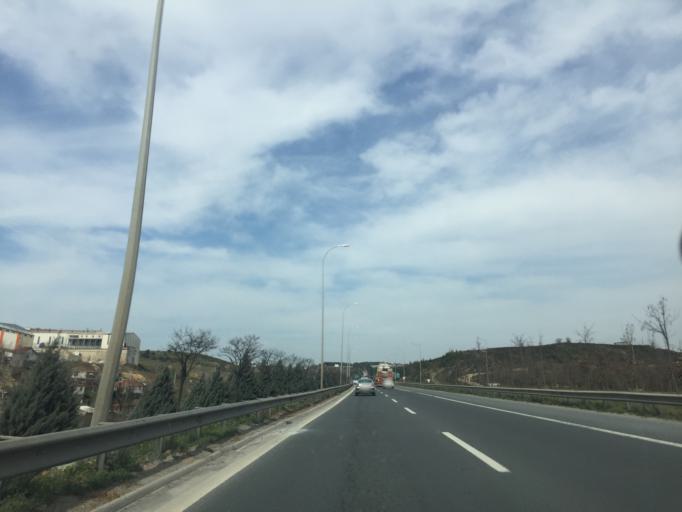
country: TR
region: Kocaeli
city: Darica
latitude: 40.8397
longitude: 29.3731
